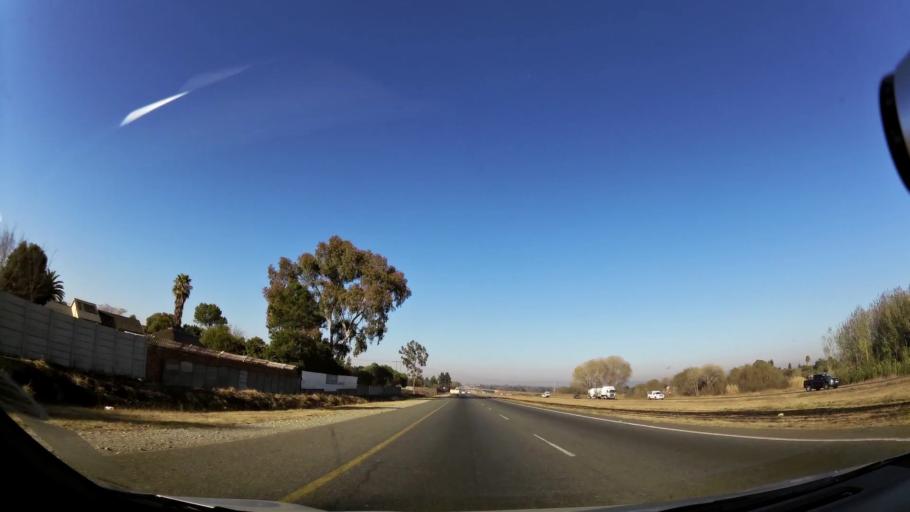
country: ZA
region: Gauteng
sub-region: Ekurhuleni Metropolitan Municipality
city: Germiston
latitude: -26.3322
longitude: 28.1103
